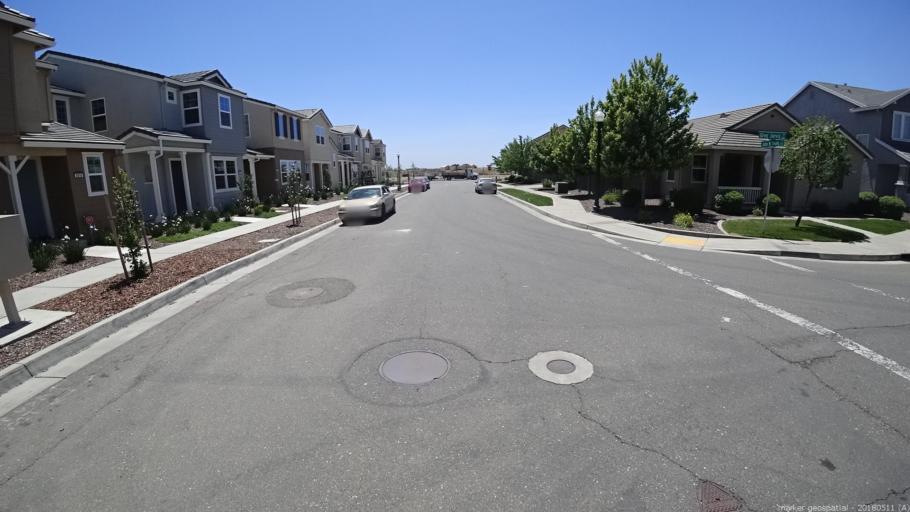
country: US
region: California
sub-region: Yolo County
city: West Sacramento
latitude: 38.6400
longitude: -121.5170
